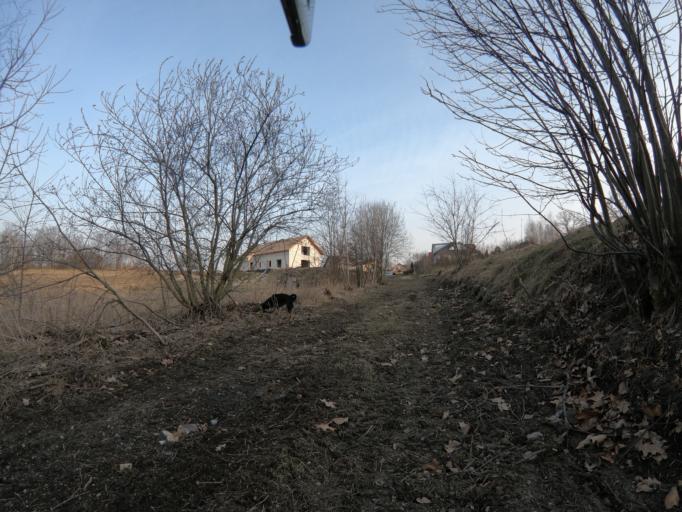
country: PL
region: Silesian Voivodeship
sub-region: Powiat raciborski
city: Pogrzebien
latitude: 50.0826
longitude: 18.2646
